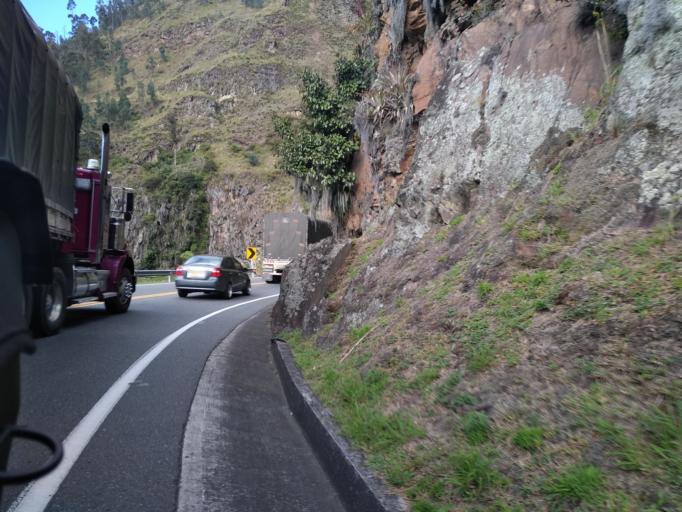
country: CO
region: Narino
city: Funes
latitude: 0.9488
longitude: -77.4730
